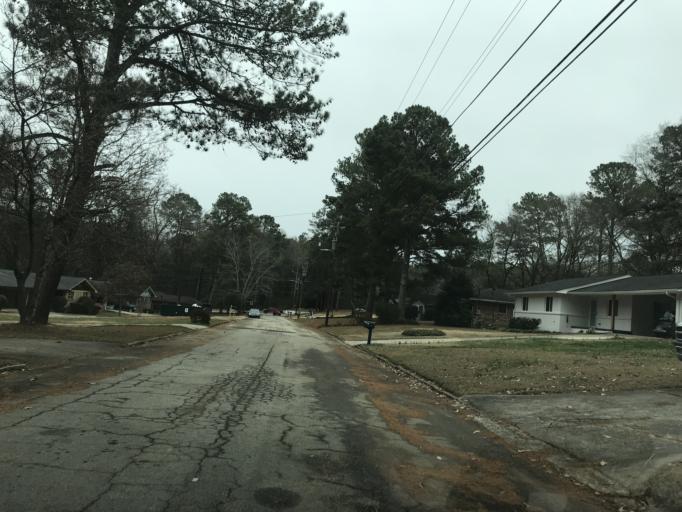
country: US
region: Georgia
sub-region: DeKalb County
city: Clarkston
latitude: 33.8330
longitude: -84.2474
